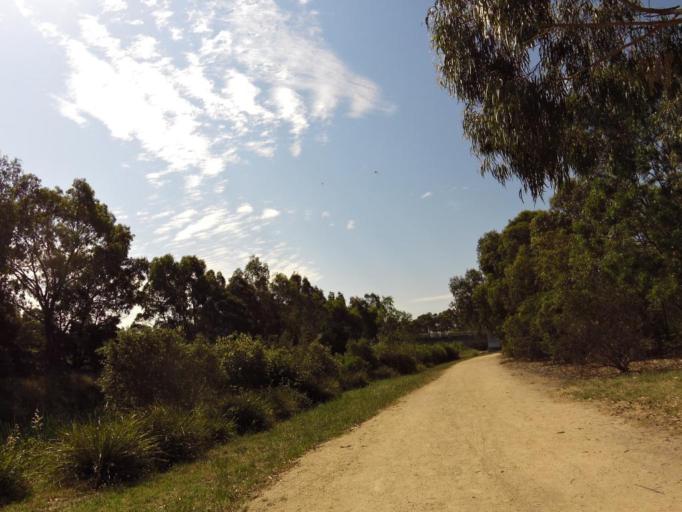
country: AU
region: Victoria
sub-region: Whittlesea
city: Epping
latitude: -37.6462
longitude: 145.0322
